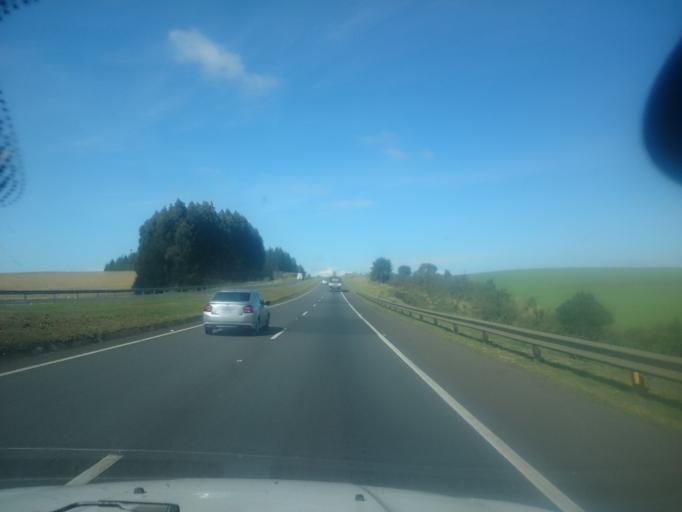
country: BR
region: Parana
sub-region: Palmeira
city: Palmeira
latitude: -25.3544
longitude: -49.8356
